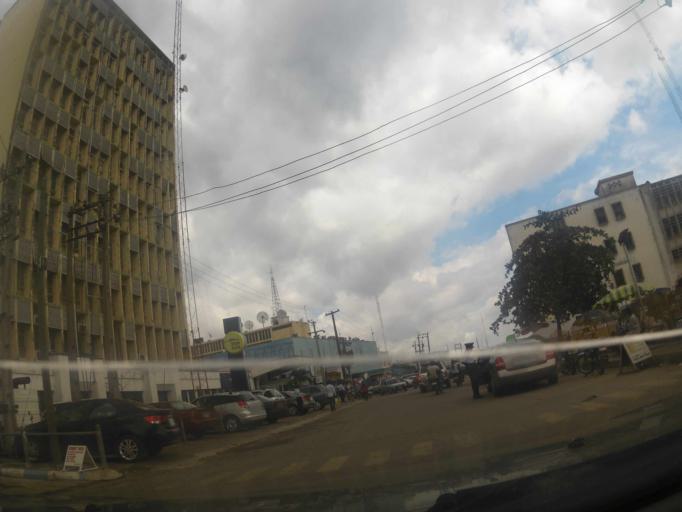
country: NG
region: Oyo
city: Ibadan
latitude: 7.3875
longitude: 3.8804
